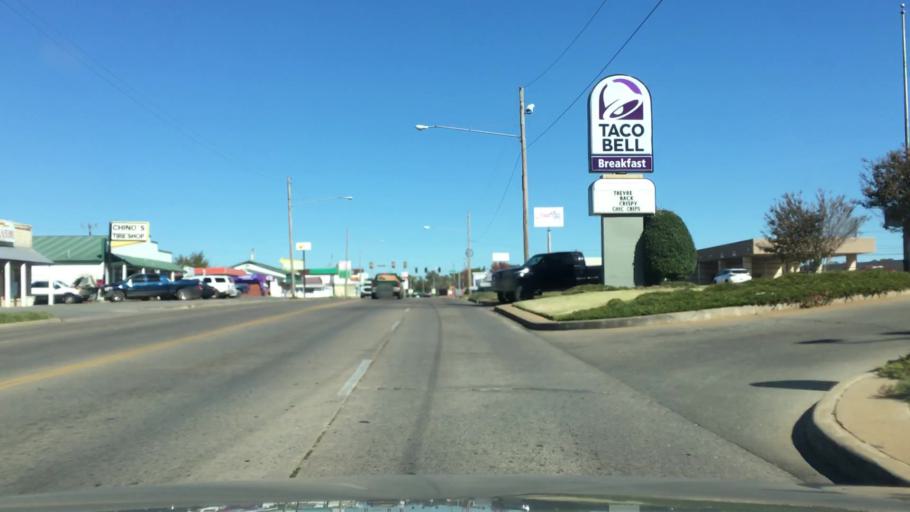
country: US
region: Oklahoma
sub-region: Cherokee County
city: Tahlequah
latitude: 35.8991
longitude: -94.9755
